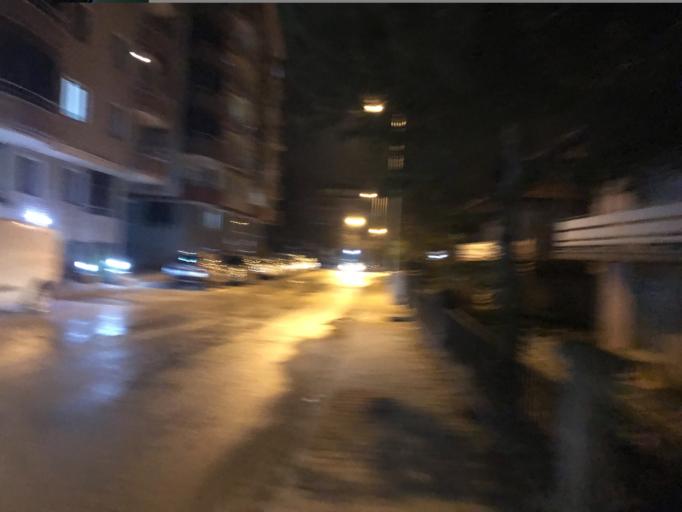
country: TR
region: Karabuk
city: Safranbolu
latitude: 41.2579
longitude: 32.6774
